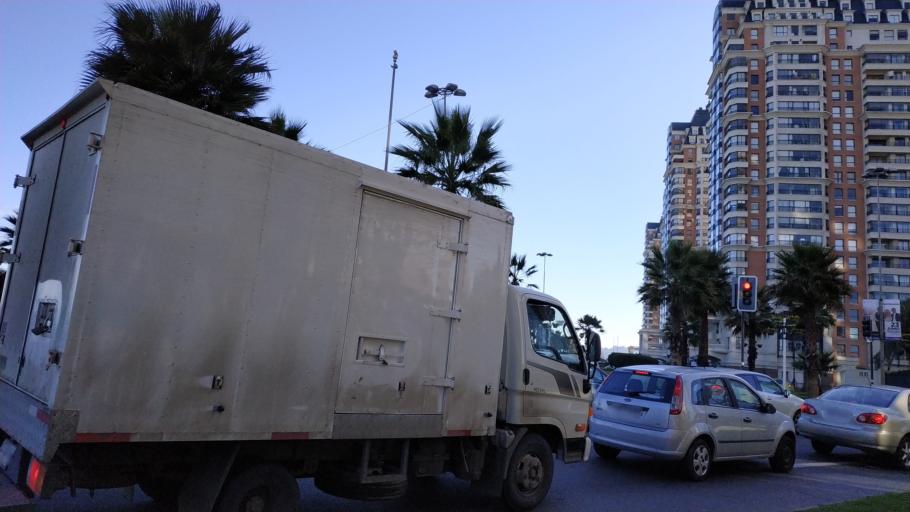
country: CL
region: Valparaiso
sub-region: Provincia de Valparaiso
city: Vina del Mar
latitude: -33.0081
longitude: -71.5508
